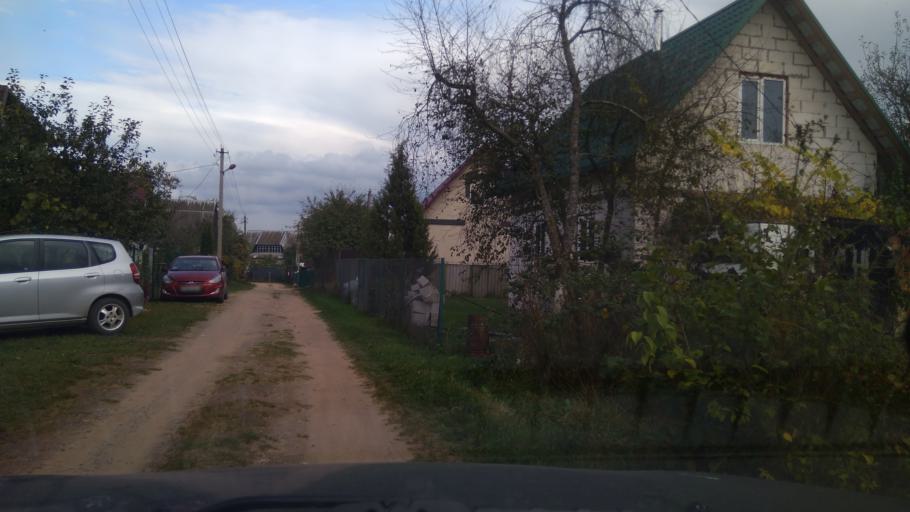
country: BY
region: Minsk
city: Rudzyensk
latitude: 53.6057
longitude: 27.8471
